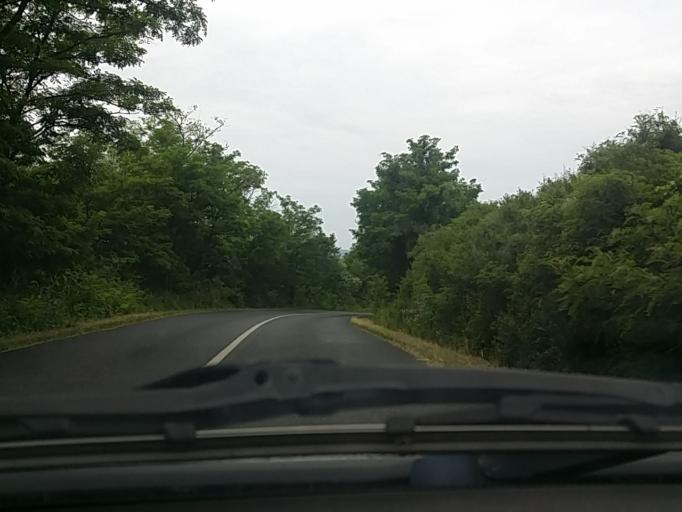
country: HU
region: Pest
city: Csobanka
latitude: 47.6263
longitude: 18.9499
